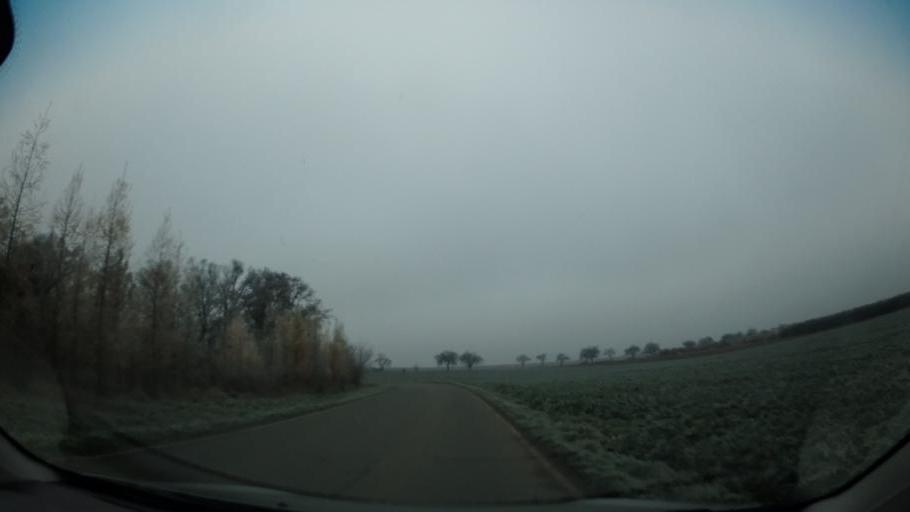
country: CZ
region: Vysocina
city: Mohelno
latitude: 49.1359
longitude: 16.2001
